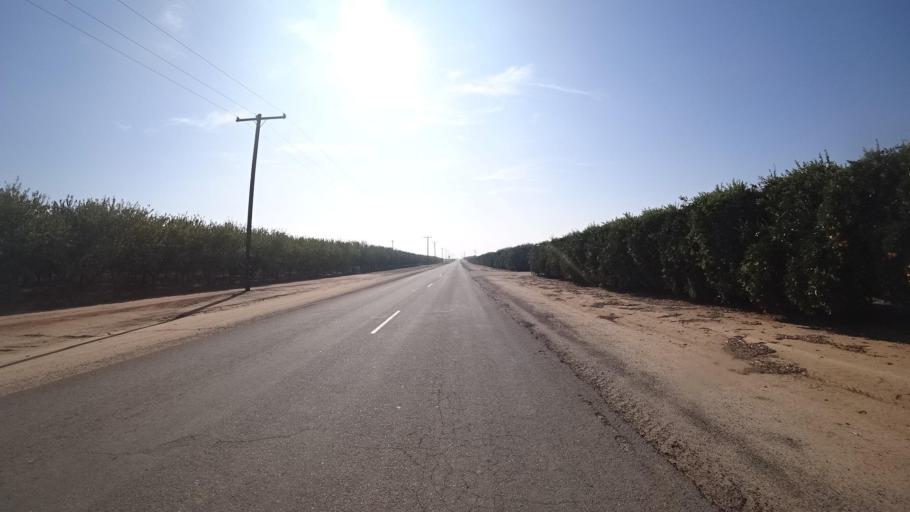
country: US
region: California
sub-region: Kern County
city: McFarland
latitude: 35.6690
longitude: -119.1692
